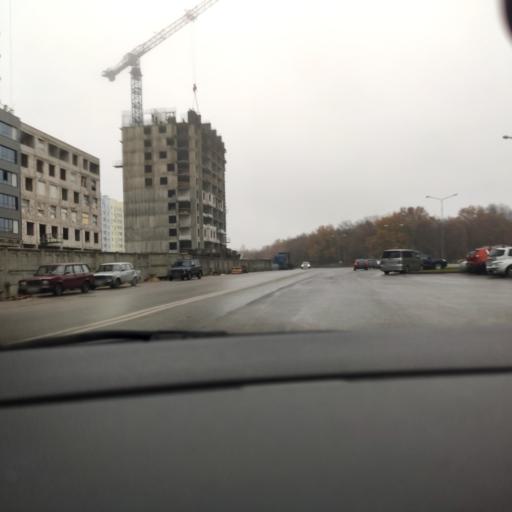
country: RU
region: Voronezj
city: Voronezh
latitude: 51.7151
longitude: 39.1922
